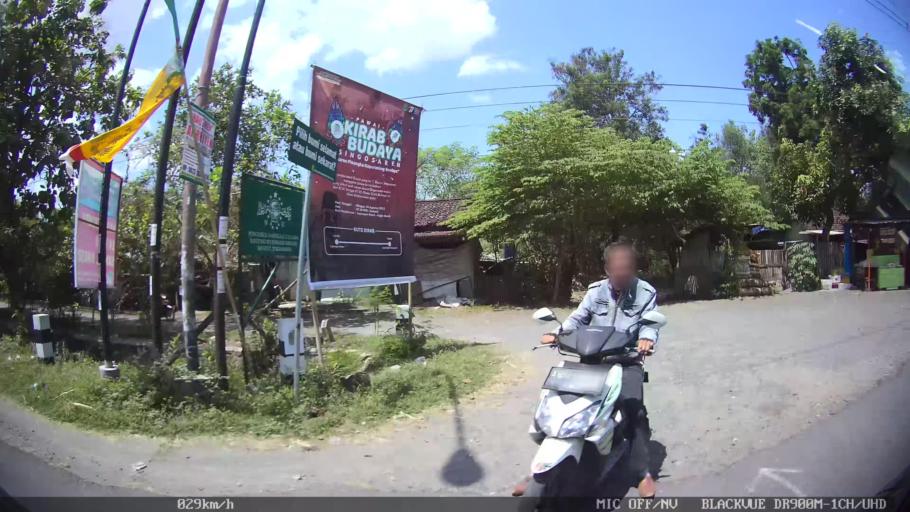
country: ID
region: Daerah Istimewa Yogyakarta
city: Sewon
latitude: -7.9048
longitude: 110.3840
